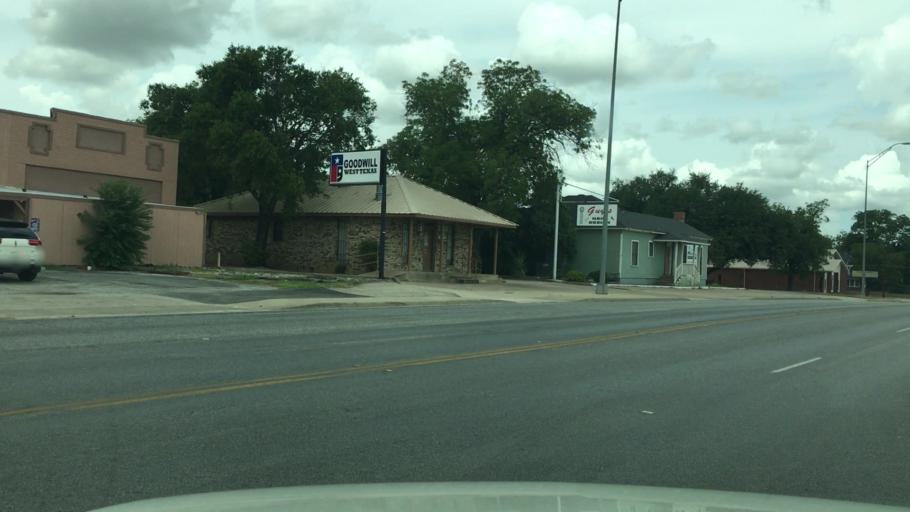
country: US
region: Texas
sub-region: McCulloch County
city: Brady
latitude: 31.1263
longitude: -99.3351
